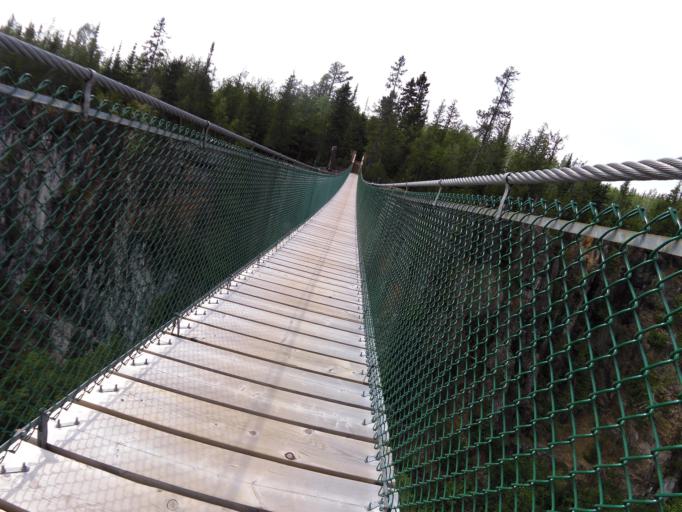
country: CA
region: Ontario
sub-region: Thunder Bay District
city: Thunder Bay
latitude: 48.7996
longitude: -88.6181
